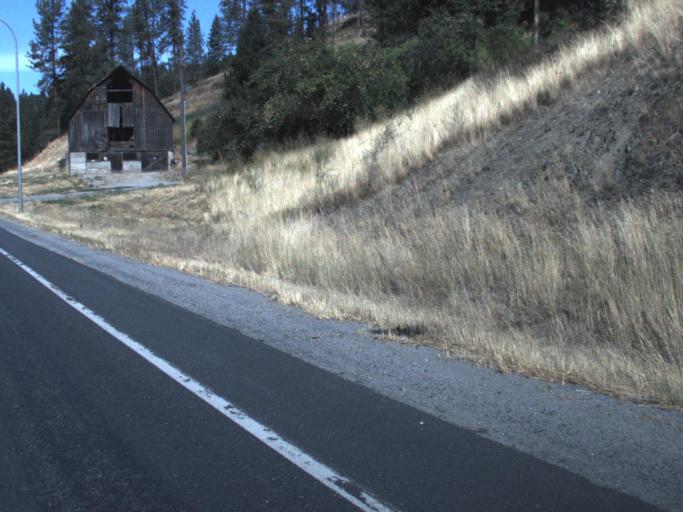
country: US
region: Washington
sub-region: Stevens County
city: Chewelah
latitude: 48.3196
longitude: -117.8183
